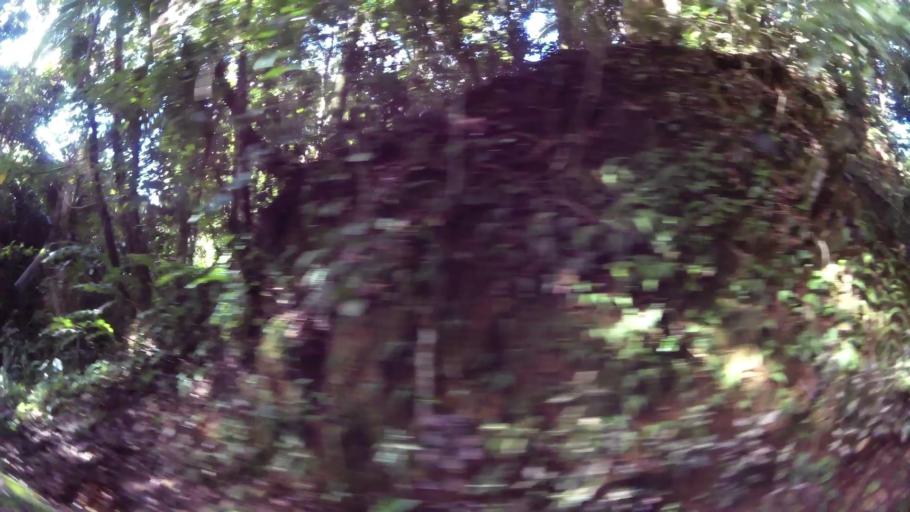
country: DM
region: Saint Andrew
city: Calibishie
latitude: 15.5923
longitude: -61.3757
